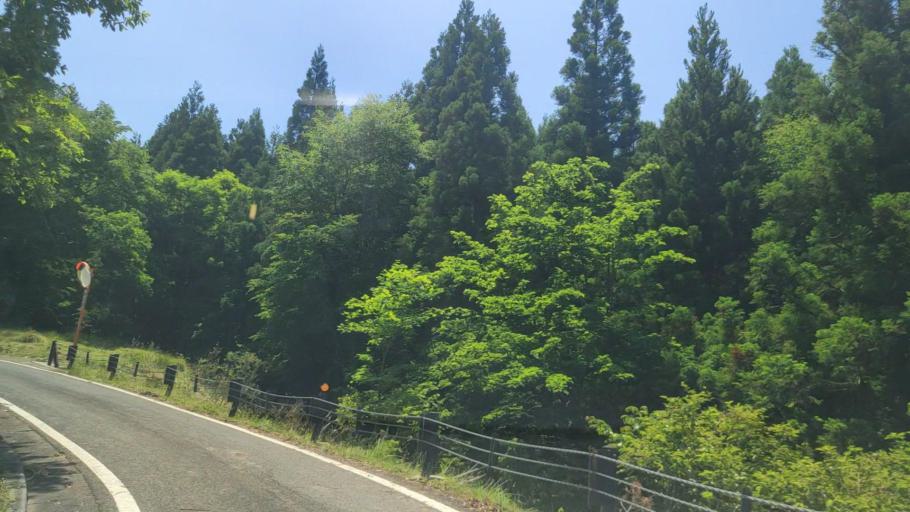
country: JP
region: Tottori
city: Tottori
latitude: 35.3703
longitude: 134.4925
